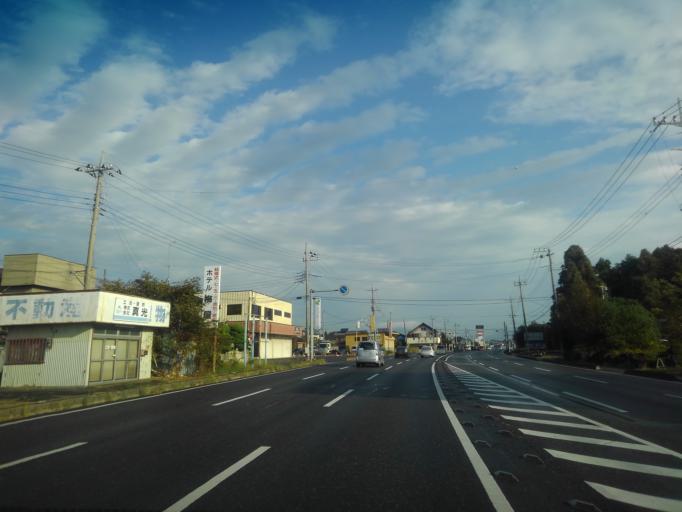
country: JP
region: Ibaraki
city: Naka
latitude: 36.0431
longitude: 140.0833
